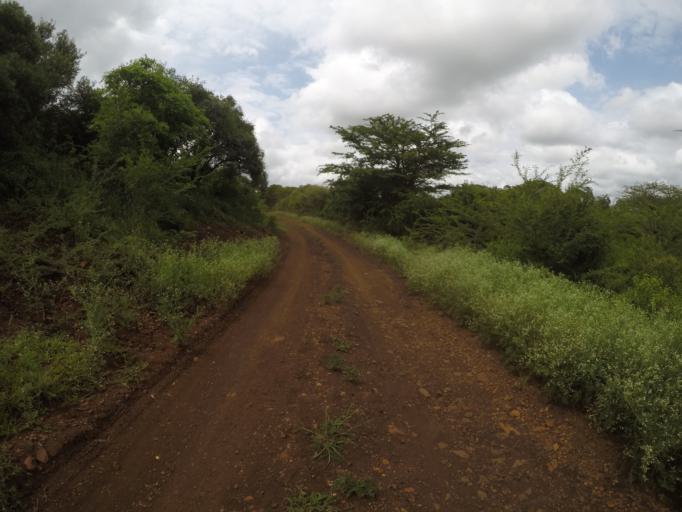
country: ZA
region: KwaZulu-Natal
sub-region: uThungulu District Municipality
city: Empangeni
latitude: -28.5905
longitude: 31.8727
